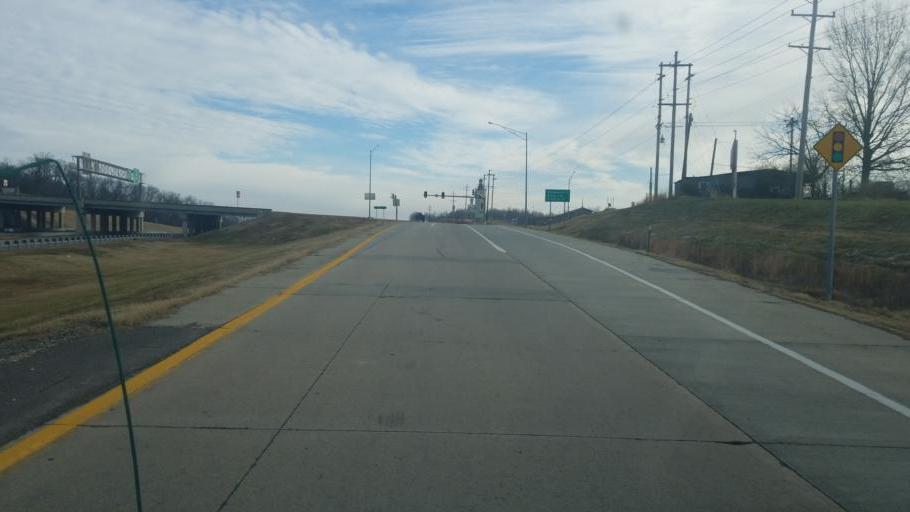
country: US
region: Missouri
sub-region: Stoddard County
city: Dexter
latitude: 36.8154
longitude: -89.9434
